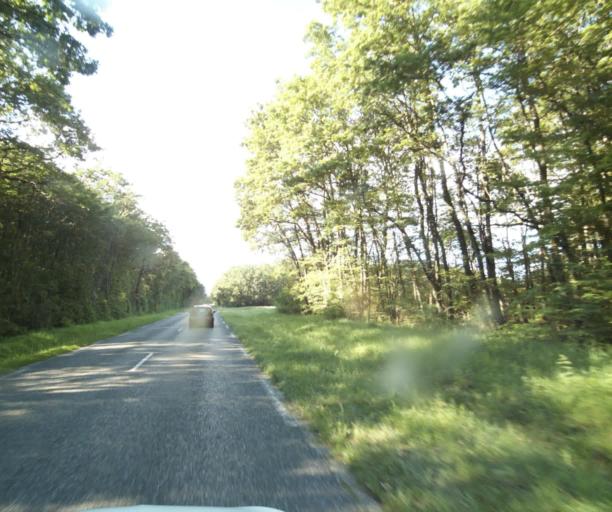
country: FR
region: Rhone-Alpes
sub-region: Departement de la Haute-Savoie
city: Messery
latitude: 46.3293
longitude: 6.2923
